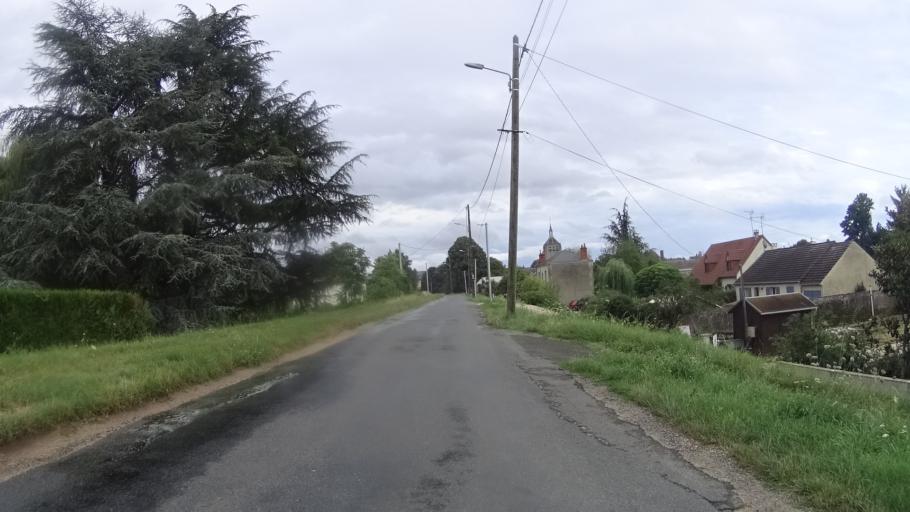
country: FR
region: Centre
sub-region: Departement du Loiret
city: Jargeau
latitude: 47.8682
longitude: 2.1174
